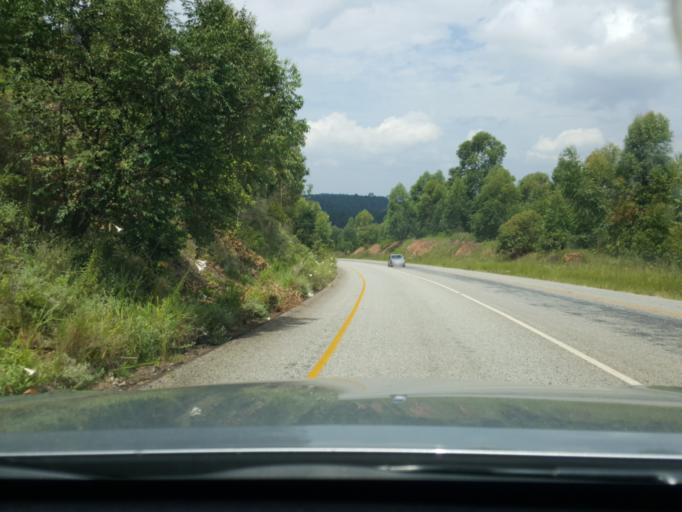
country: ZA
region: Mpumalanga
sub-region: Ehlanzeni District
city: White River
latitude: -25.1952
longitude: 30.9151
